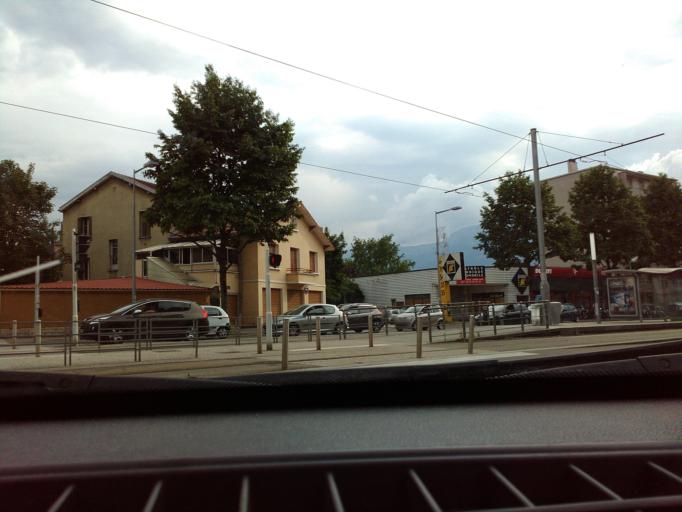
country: FR
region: Rhone-Alpes
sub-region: Departement de l'Isere
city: La Tronche
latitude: 45.1878
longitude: 5.7518
